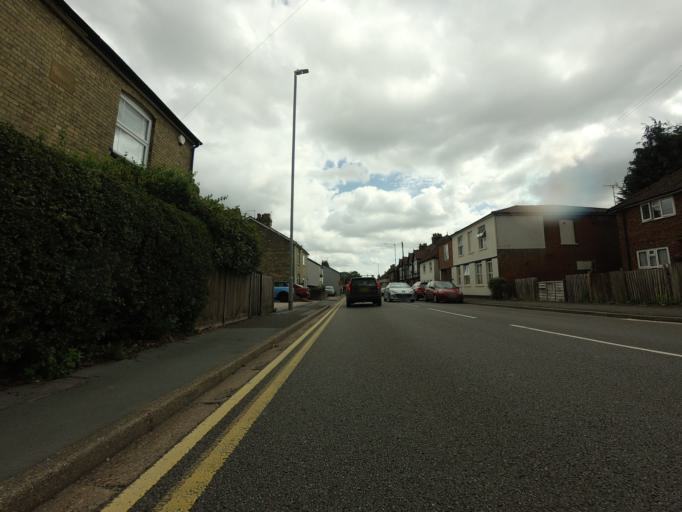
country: GB
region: England
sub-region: Kent
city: Sevenoaks
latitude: 51.2967
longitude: 0.1649
